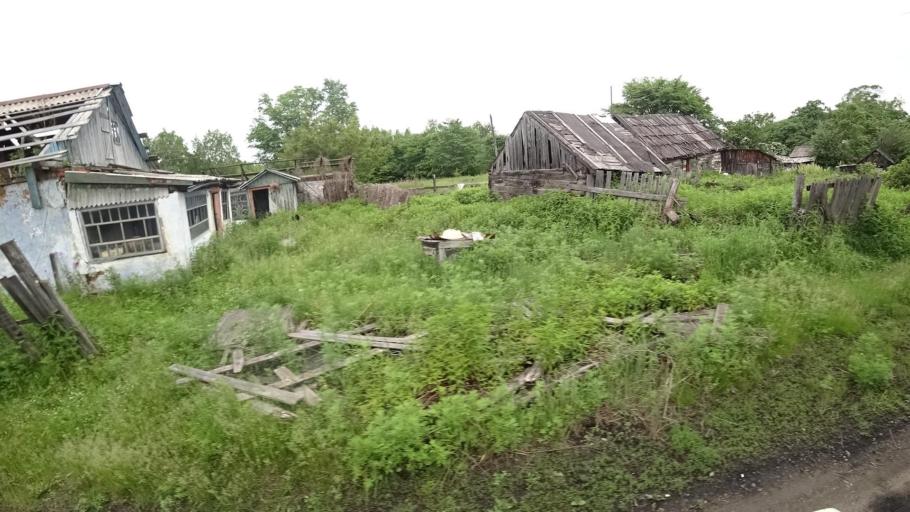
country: RU
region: Khabarovsk Krai
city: Amursk
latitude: 49.9059
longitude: 136.1326
